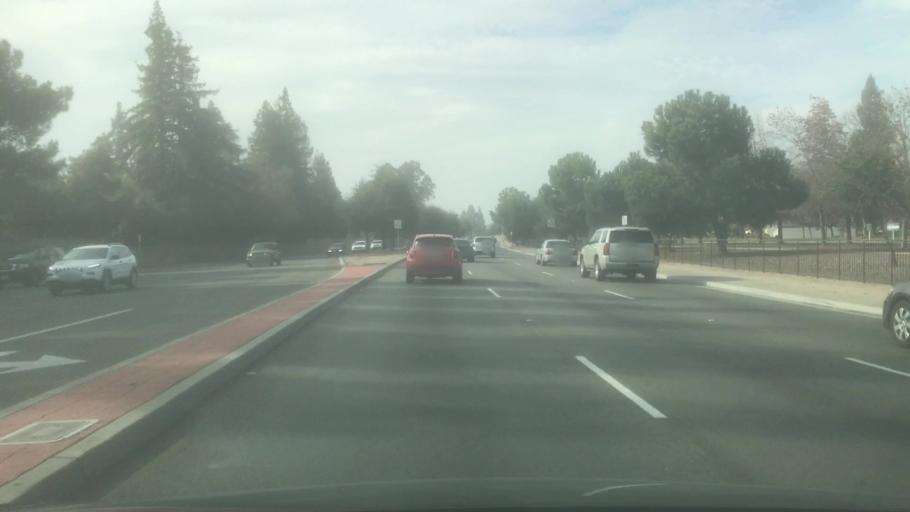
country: US
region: California
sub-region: Fresno County
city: Fresno
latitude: 36.8371
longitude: -119.8183
